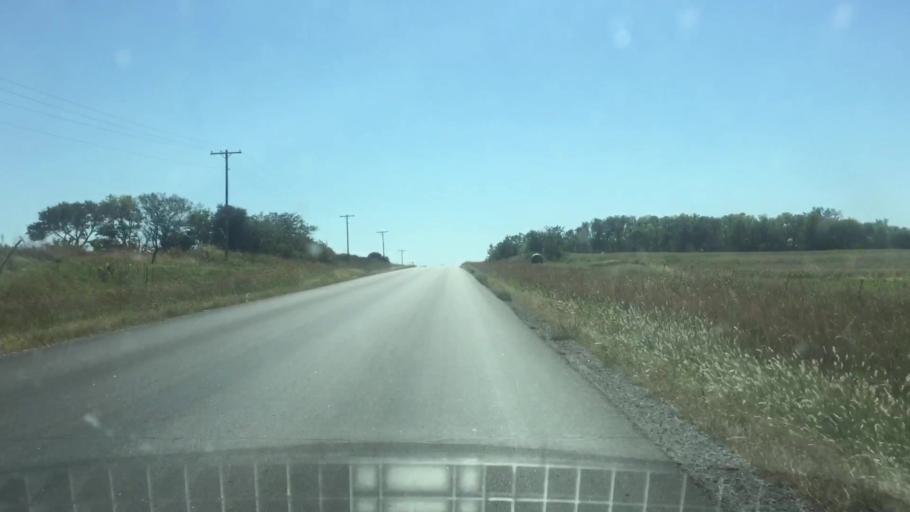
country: US
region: Kansas
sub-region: Marshall County
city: Marysville
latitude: 39.9357
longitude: -96.6009
